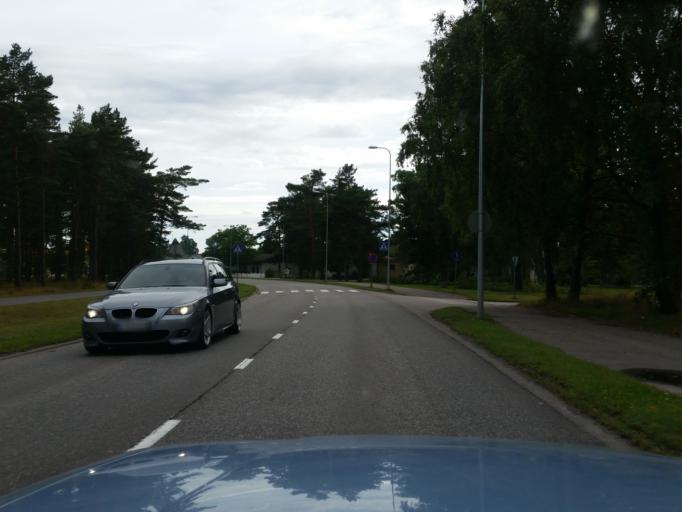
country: FI
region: Uusimaa
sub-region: Raaseporin
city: Hanko
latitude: 59.8365
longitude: 22.9926
